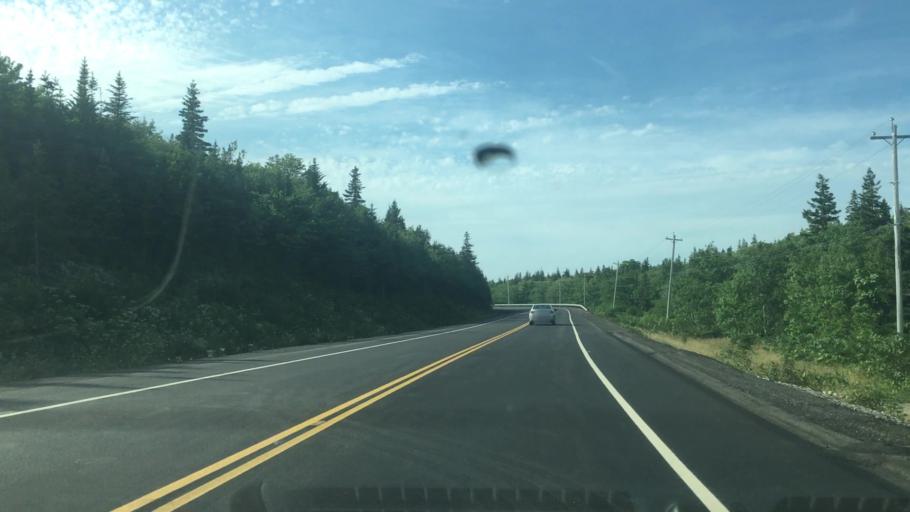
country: CA
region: Nova Scotia
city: Sydney Mines
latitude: 46.8384
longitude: -60.3860
